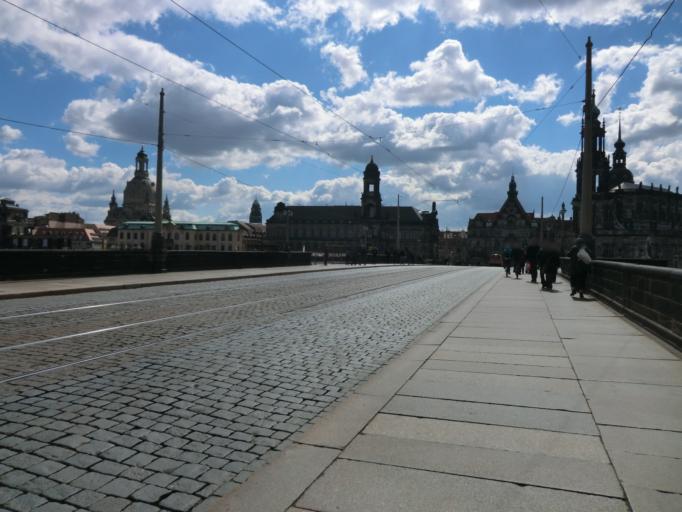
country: DE
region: Saxony
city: Dresden
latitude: 51.0556
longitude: 13.7397
